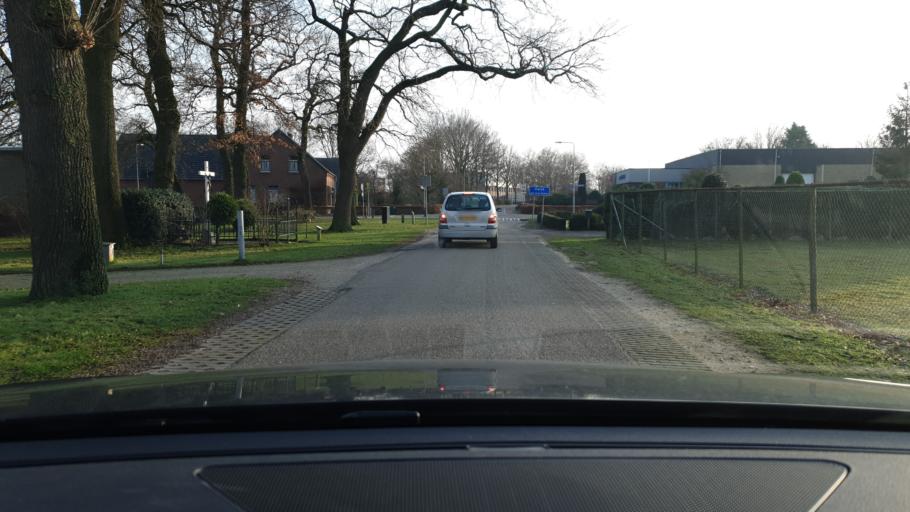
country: NL
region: Limburg
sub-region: Gemeente Venray
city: Venray
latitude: 51.4666
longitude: 6.0480
